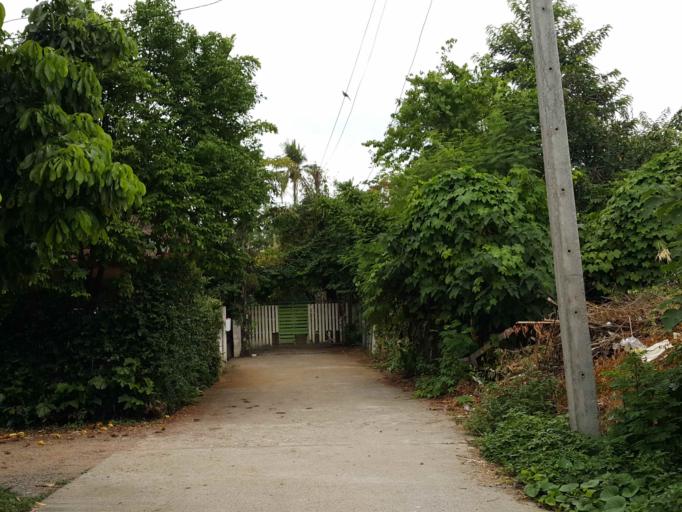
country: TH
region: Chiang Mai
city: Chiang Mai
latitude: 18.7488
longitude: 99.0011
